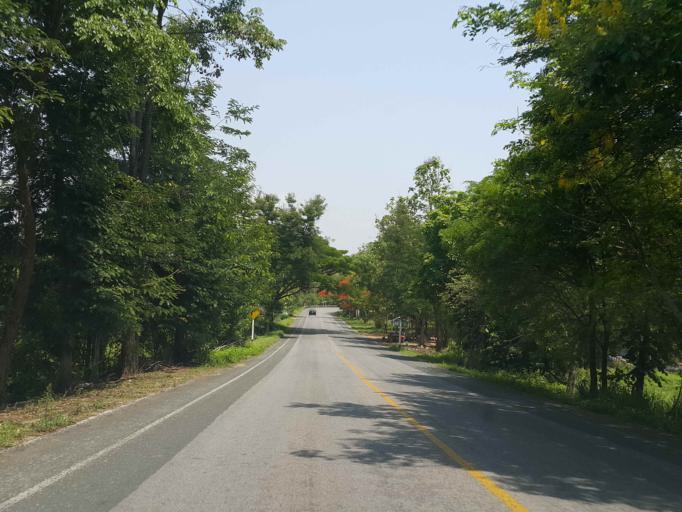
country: TH
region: Chiang Mai
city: Mae Taeng
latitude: 19.0981
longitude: 99.0008
